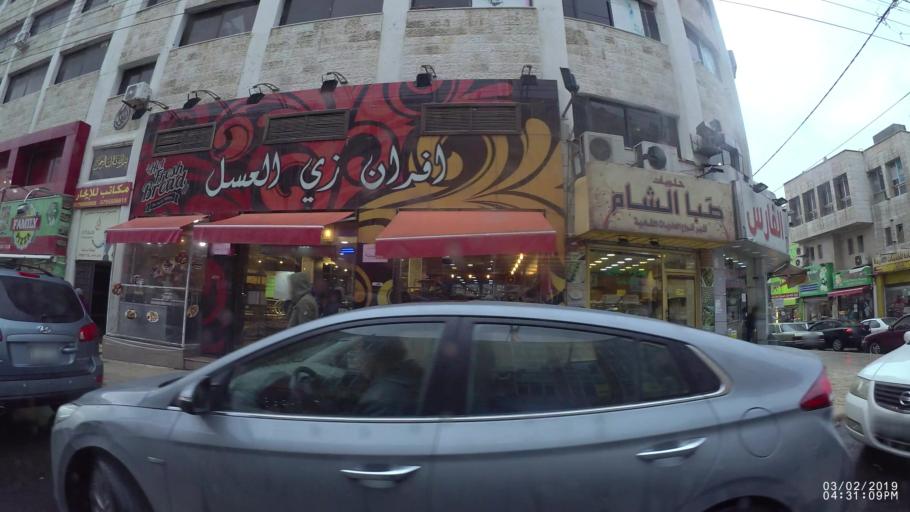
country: JO
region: Amman
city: Amman
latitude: 31.9688
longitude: 35.9192
